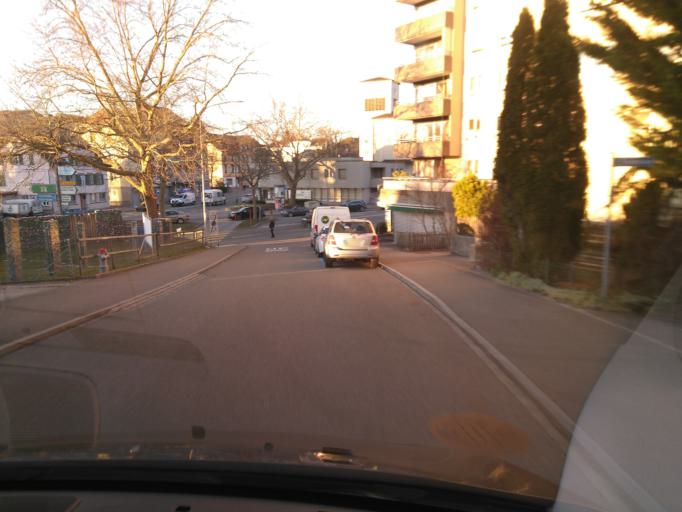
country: CH
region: Saint Gallen
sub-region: Wahlkreis St. Gallen
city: Sankt Gallen
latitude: 47.4085
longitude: 9.3311
